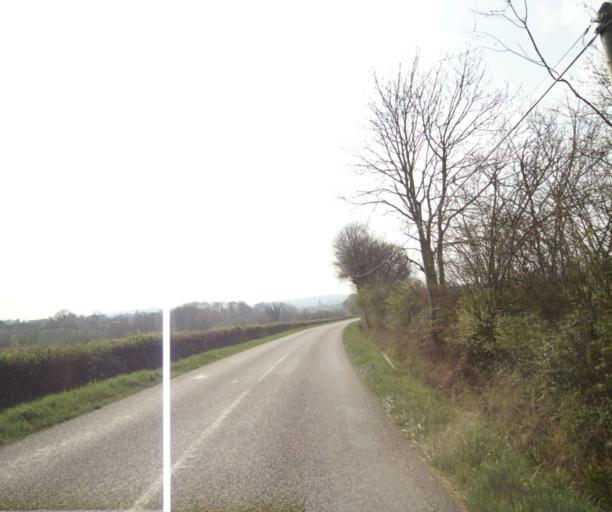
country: FR
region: Bourgogne
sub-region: Departement de Saone-et-Loire
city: Charolles
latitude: 46.4823
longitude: 4.4529
